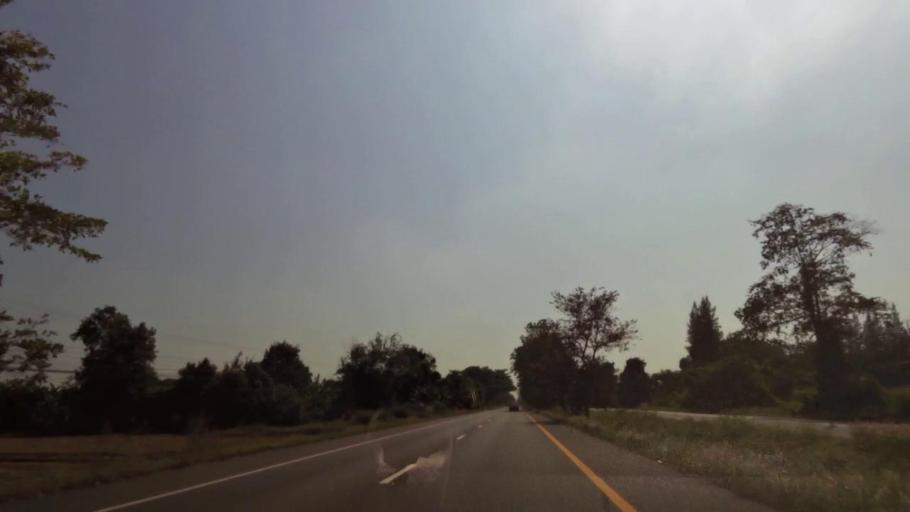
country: TH
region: Nakhon Sawan
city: Banphot Phisai
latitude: 16.0035
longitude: 100.1160
